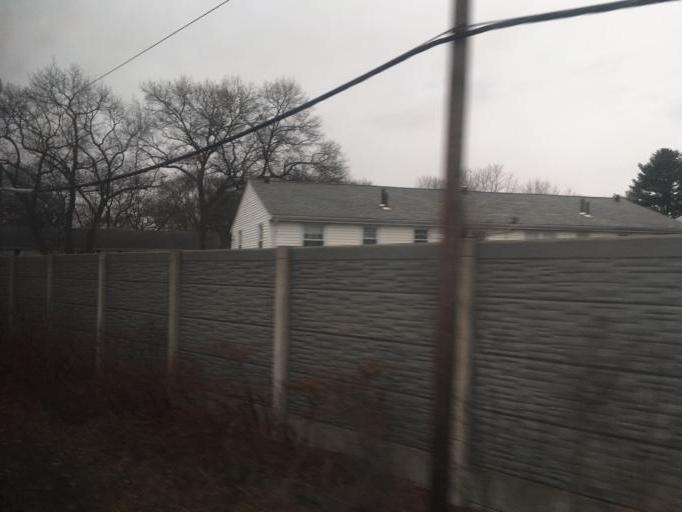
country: US
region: Massachusetts
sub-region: Norfolk County
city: Dedham
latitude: 42.2308
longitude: -71.1372
